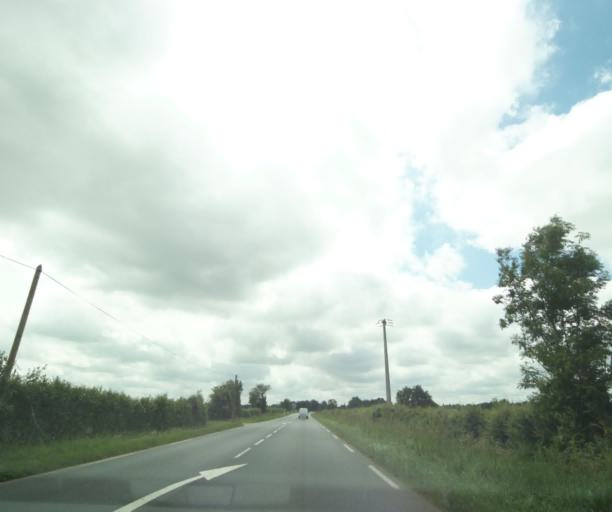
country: FR
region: Poitou-Charentes
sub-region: Departement des Deux-Sevres
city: Viennay
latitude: 46.7063
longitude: -0.2391
